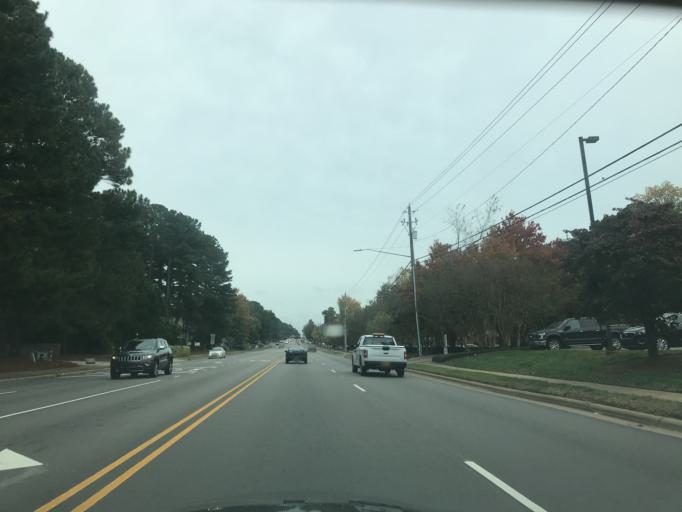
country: US
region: North Carolina
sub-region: Wake County
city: West Raleigh
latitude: 35.8796
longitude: -78.6251
